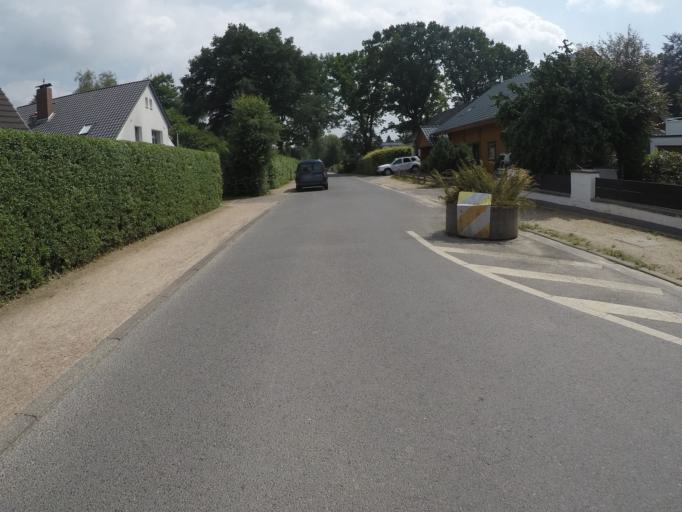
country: DE
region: Hamburg
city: Sasel
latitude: 53.6458
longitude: 10.1166
